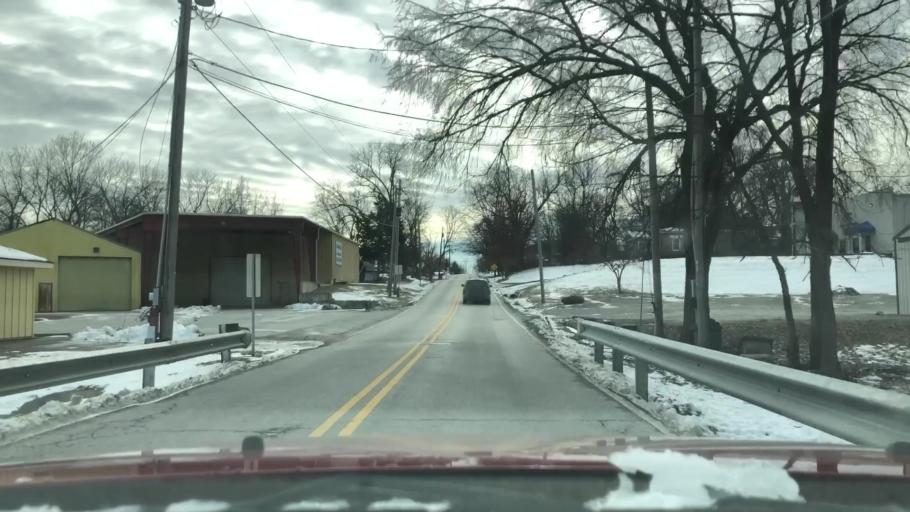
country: US
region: Missouri
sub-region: Jackson County
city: Greenwood
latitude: 38.8540
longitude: -94.3437
